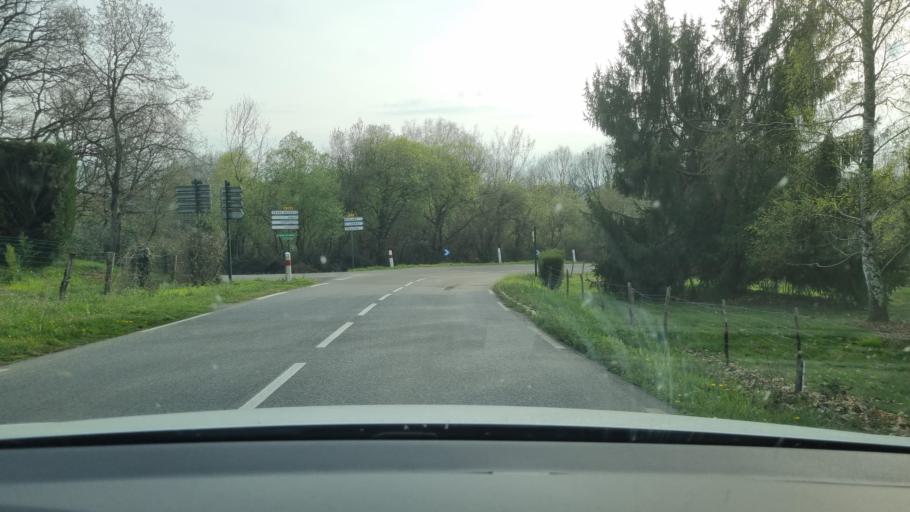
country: FR
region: Aquitaine
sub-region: Departement des Pyrenees-Atlantiques
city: Morlaas
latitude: 43.3661
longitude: -0.1939
